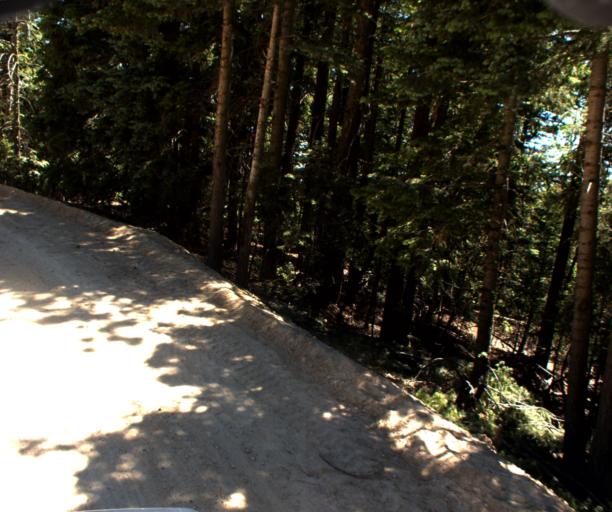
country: US
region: Arizona
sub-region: Graham County
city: Swift Trail Junction
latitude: 32.6605
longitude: -109.8661
